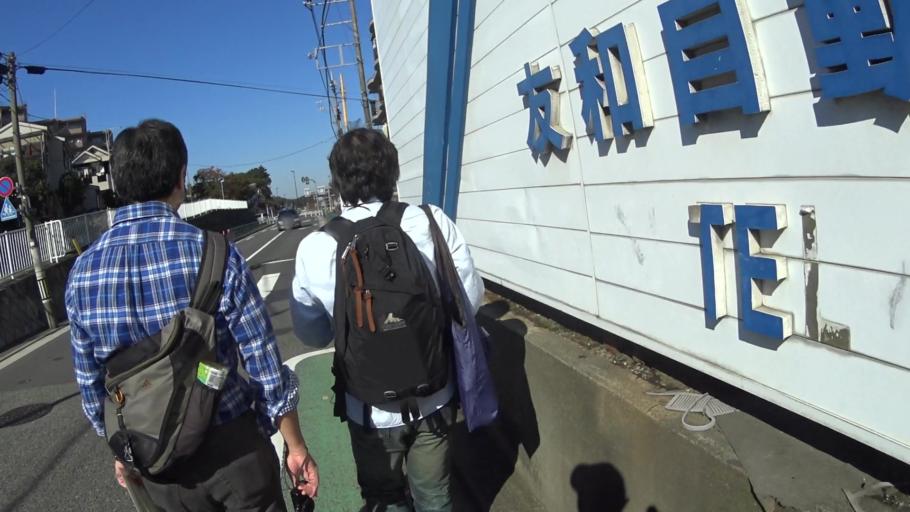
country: JP
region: Tokyo
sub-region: Machida-shi
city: Machida
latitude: 35.5563
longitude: 139.4487
